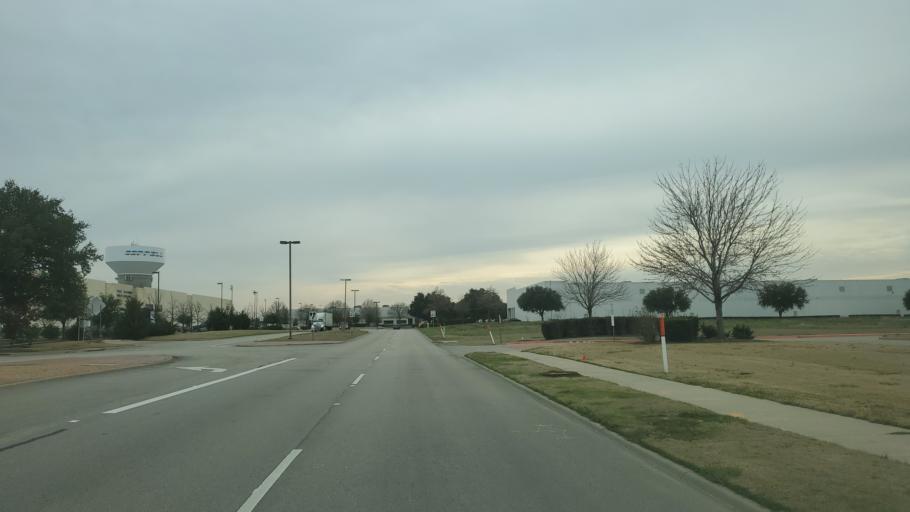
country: US
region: Texas
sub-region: Dallas County
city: Coppell
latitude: 32.9709
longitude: -97.0251
